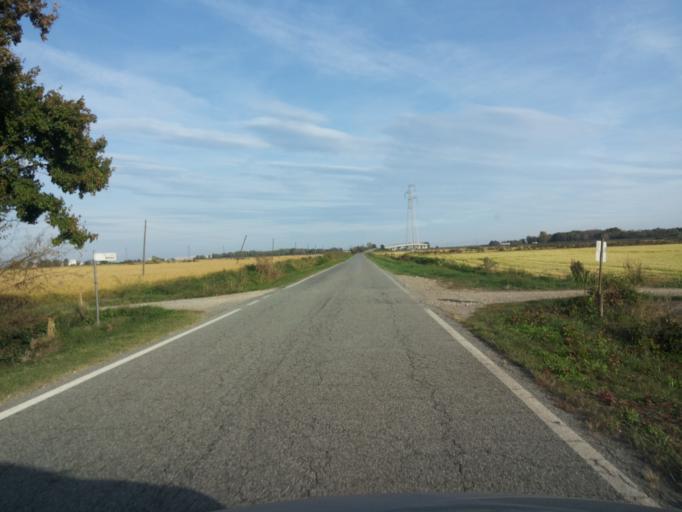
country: IT
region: Piedmont
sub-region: Provincia di Vercelli
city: Carisio
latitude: 45.4306
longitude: 8.1839
